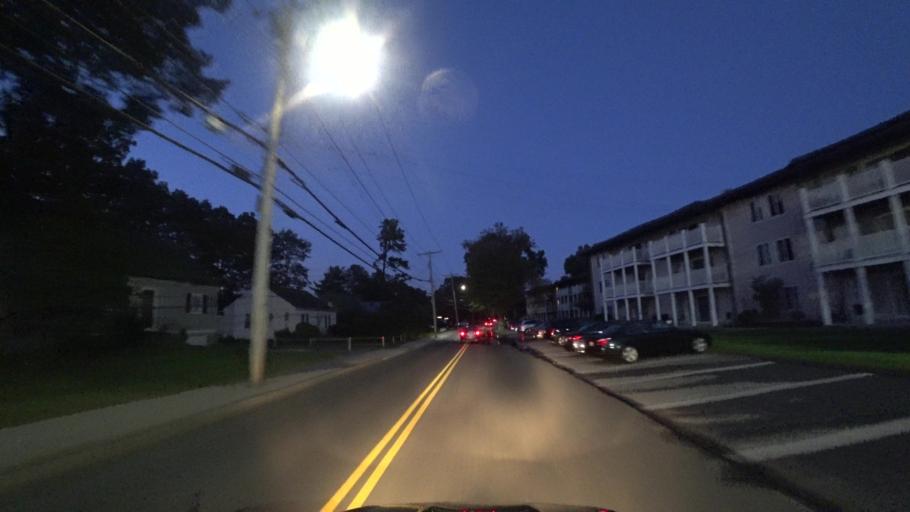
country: US
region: Massachusetts
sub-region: Middlesex County
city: Woburn
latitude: 42.5002
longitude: -71.1659
